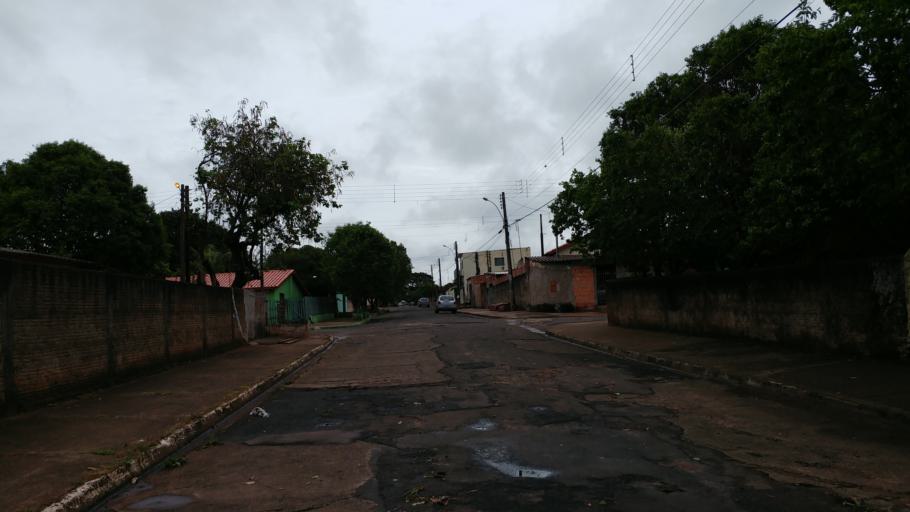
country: BR
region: Sao Paulo
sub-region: Paraguacu Paulista
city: Paraguacu Paulista
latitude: -22.4105
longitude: -50.5658
